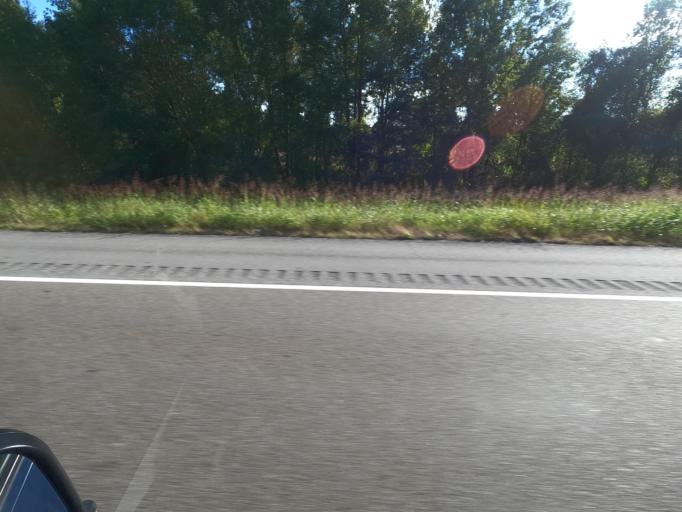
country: US
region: Tennessee
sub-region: Madison County
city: Jackson
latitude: 35.6681
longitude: -88.9114
